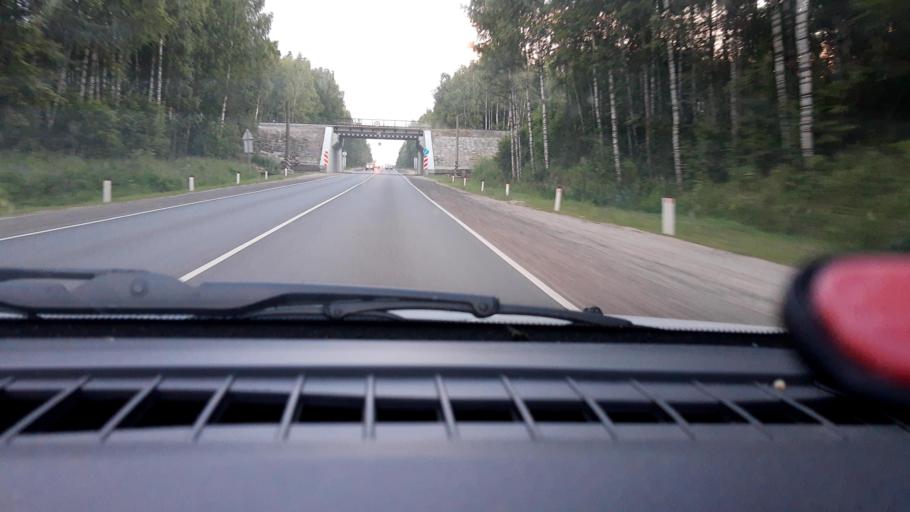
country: RU
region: Nizjnij Novgorod
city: Arzamas
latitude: 55.4305
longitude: 43.9017
